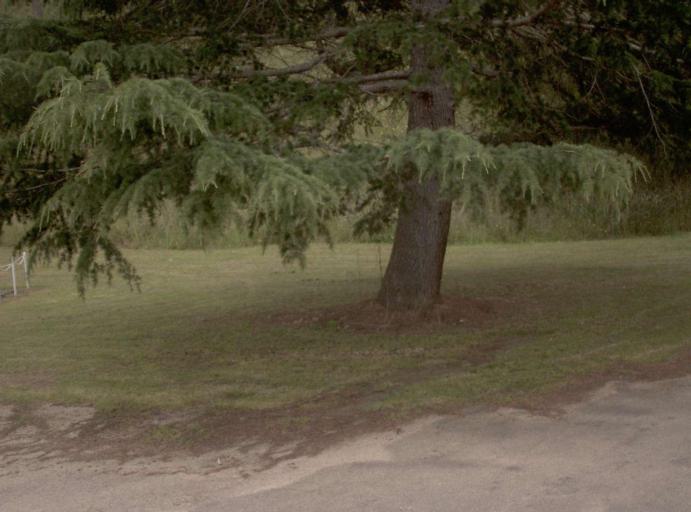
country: AU
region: Victoria
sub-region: East Gippsland
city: Bairnsdale
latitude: -37.4555
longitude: 147.2512
